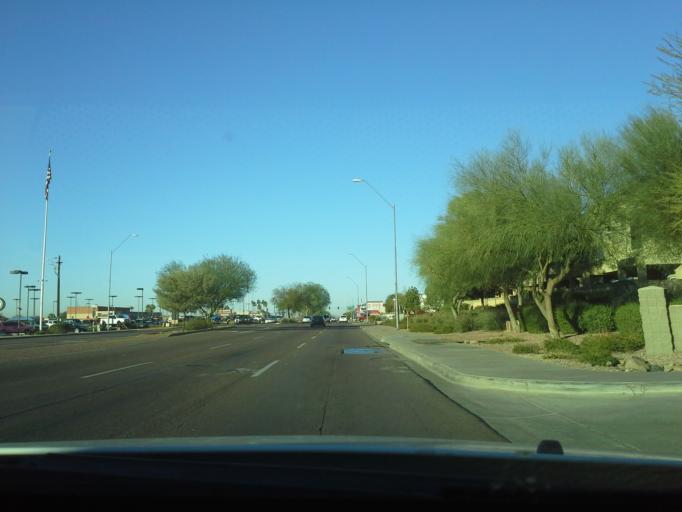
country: US
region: Arizona
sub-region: Maricopa County
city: Paradise Valley
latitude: 33.6406
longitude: -112.0363
